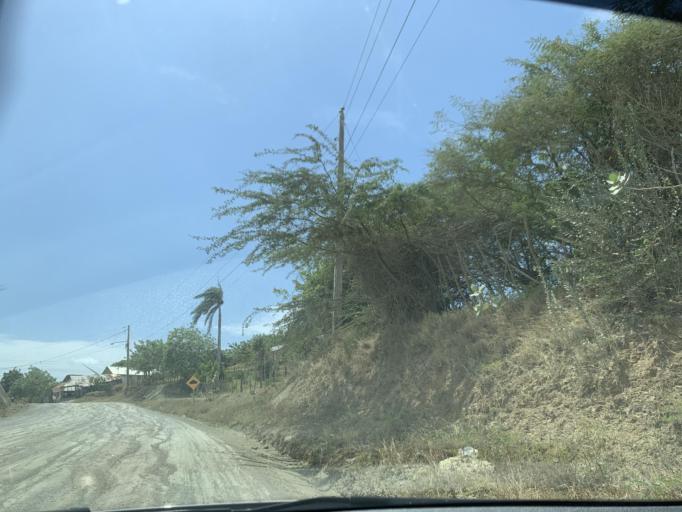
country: DO
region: Puerto Plata
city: Imbert
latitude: 19.8667
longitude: -70.8135
